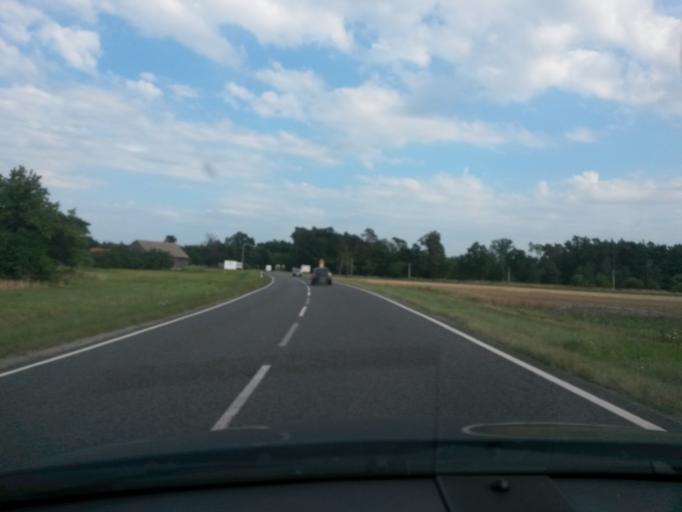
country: PL
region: Greater Poland Voivodeship
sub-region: Powiat rawicki
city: Rawicz
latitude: 51.5757
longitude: 16.8729
